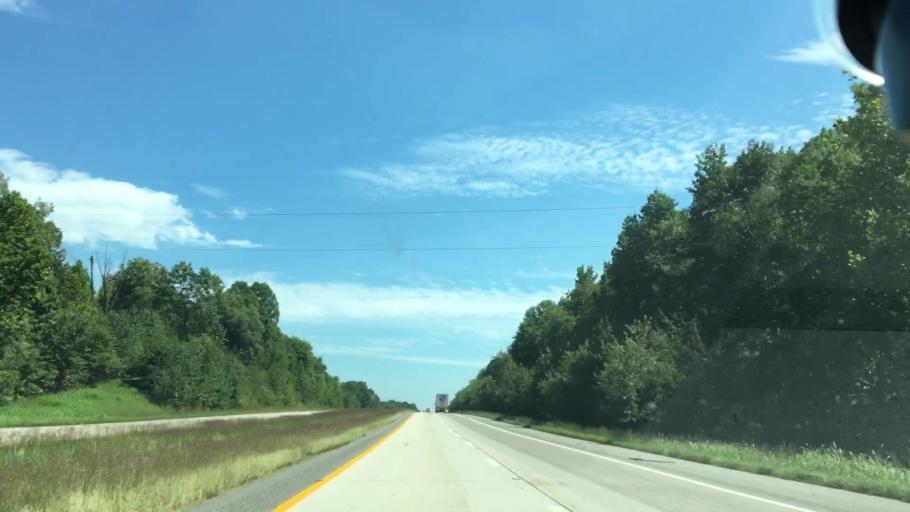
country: US
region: Kentucky
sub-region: Henderson County
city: Henderson
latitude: 37.7793
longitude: -87.4515
